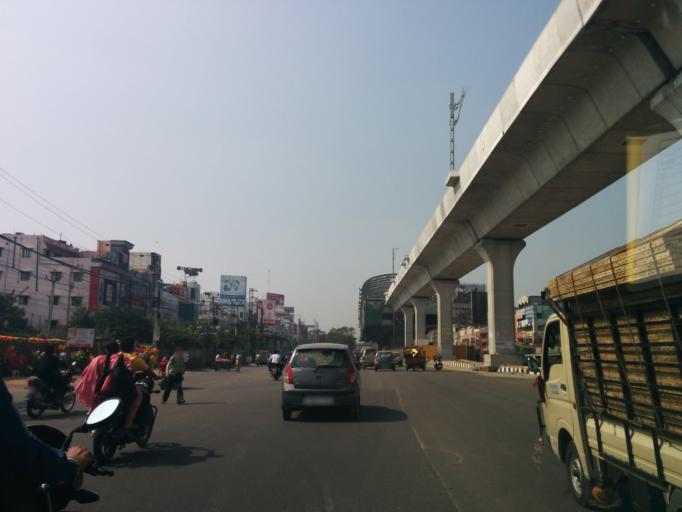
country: IN
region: Telangana
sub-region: Rangareddi
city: Kukatpalli
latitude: 17.4927
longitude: 78.4037
